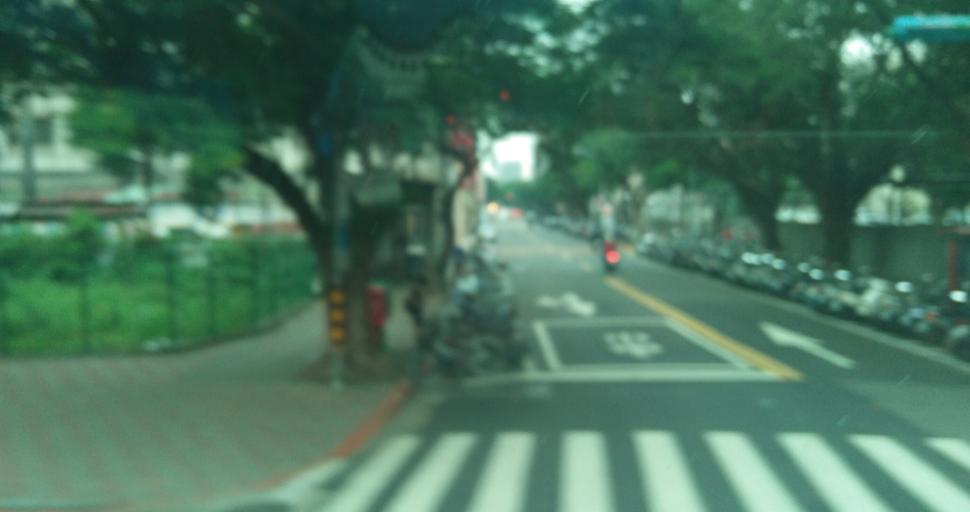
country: TW
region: Taipei
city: Taipei
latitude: 25.0371
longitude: 121.5081
